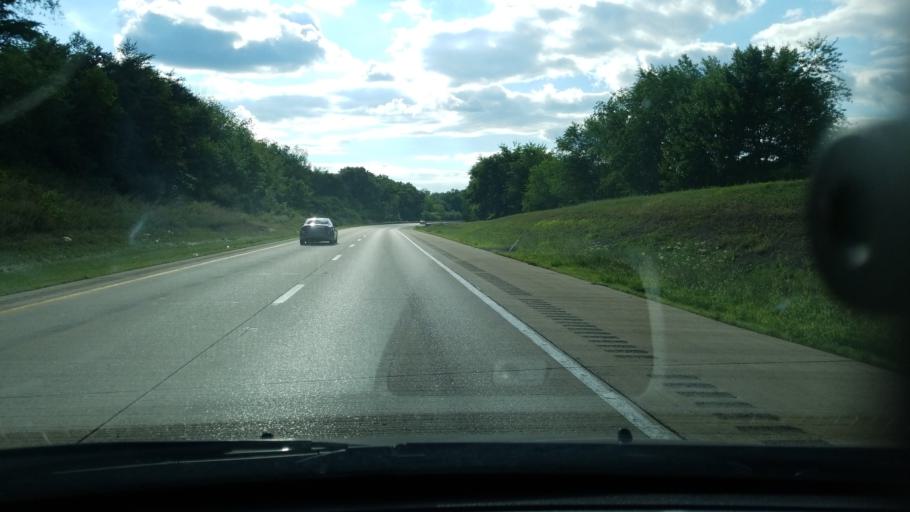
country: US
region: Pennsylvania
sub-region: Northumberland County
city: Milton
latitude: 40.9930
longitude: -76.7368
